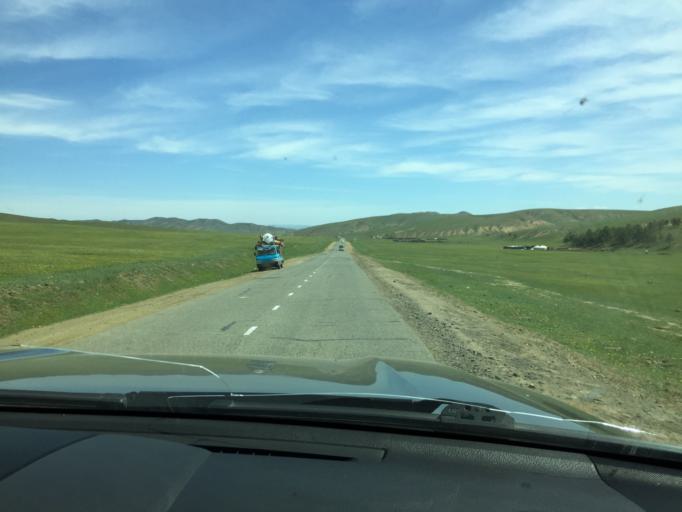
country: MN
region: Central Aimak
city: Javhlant
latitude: 48.6593
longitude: 106.1195
